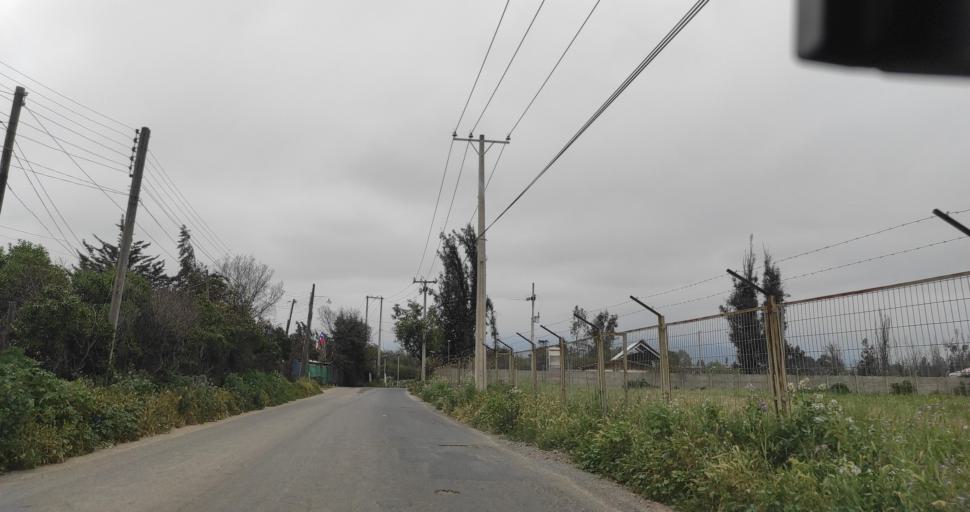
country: CL
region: Valparaiso
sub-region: Provincia de Marga Marga
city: Limache
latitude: -32.9983
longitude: -71.2343
